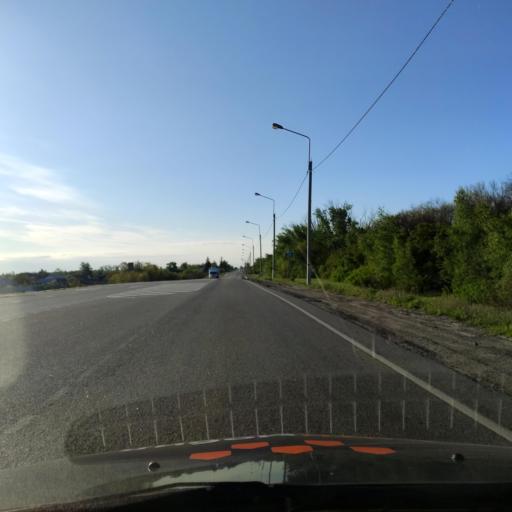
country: RU
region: Lipetsk
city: Yelets
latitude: 52.5605
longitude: 38.6874
